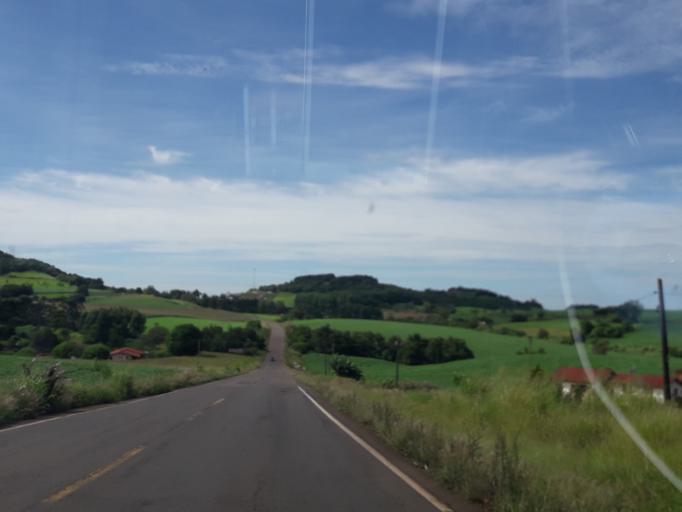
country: AR
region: Misiones
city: Bernardo de Irigoyen
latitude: -26.3629
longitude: -53.5348
